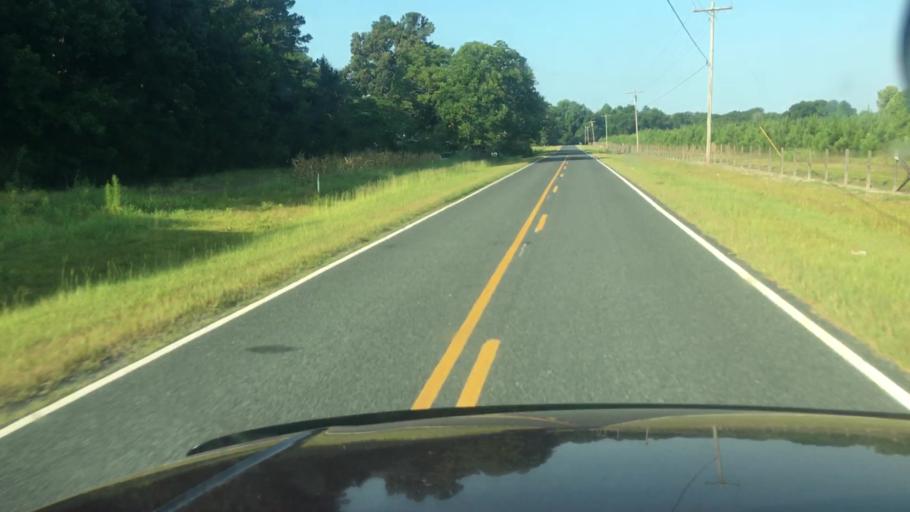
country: US
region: North Carolina
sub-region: Robeson County
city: Saint Pauls
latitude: 34.8405
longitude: -78.8907
